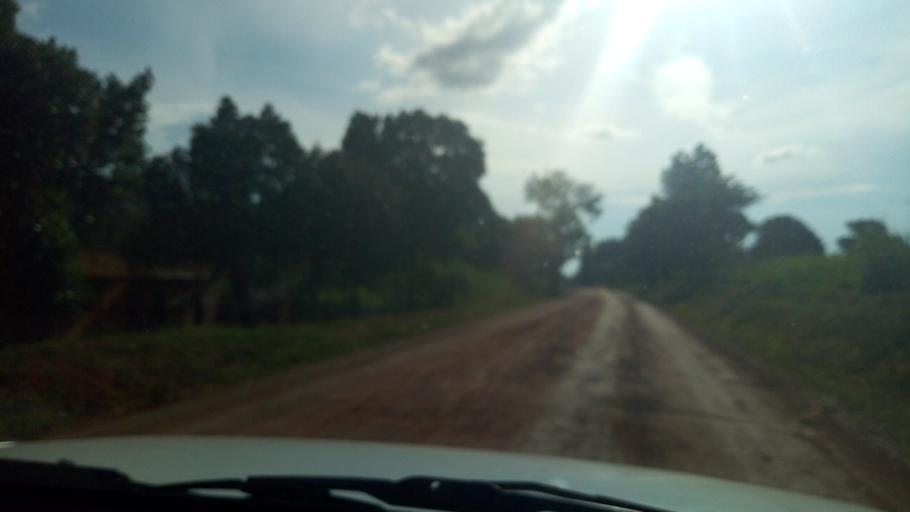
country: UG
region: Western Region
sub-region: Masindi District
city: Masindi
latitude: 1.6753
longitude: 31.6656
